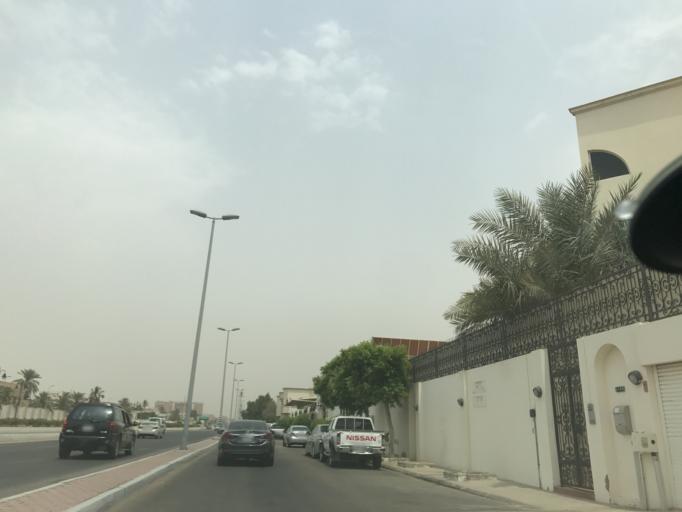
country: SA
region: Makkah
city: Jeddah
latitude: 21.5548
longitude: 39.1618
